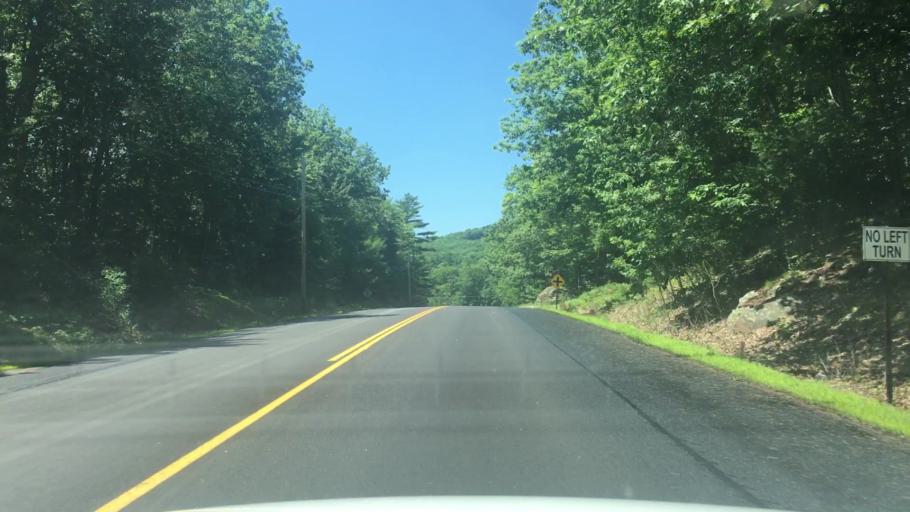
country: US
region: Maine
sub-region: Waldo County
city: Searsmont
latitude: 44.4012
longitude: -69.2868
